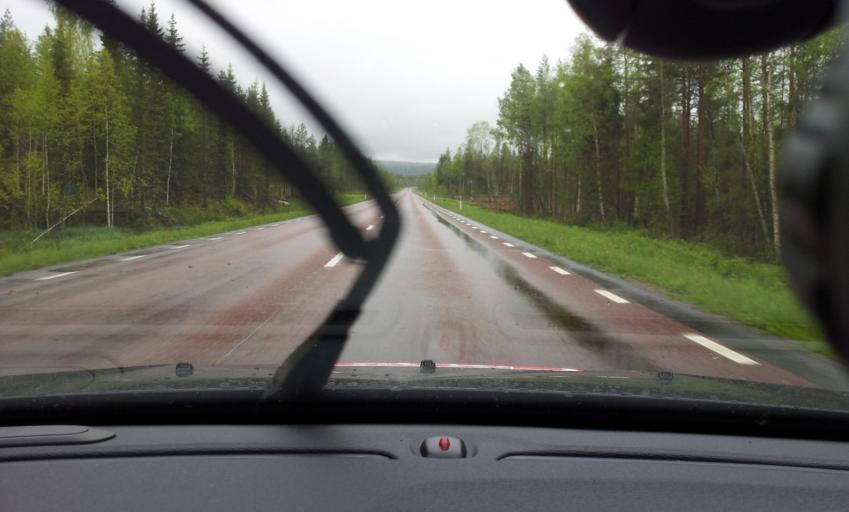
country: SE
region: Jaemtland
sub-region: Bergs Kommun
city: Hoverberg
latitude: 62.8207
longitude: 14.5163
